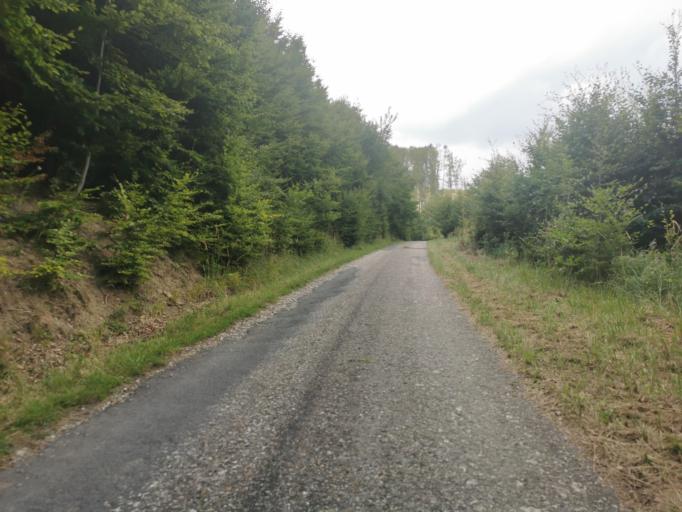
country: SK
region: Nitriansky
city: Stara Tura
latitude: 48.8331
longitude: 17.6237
